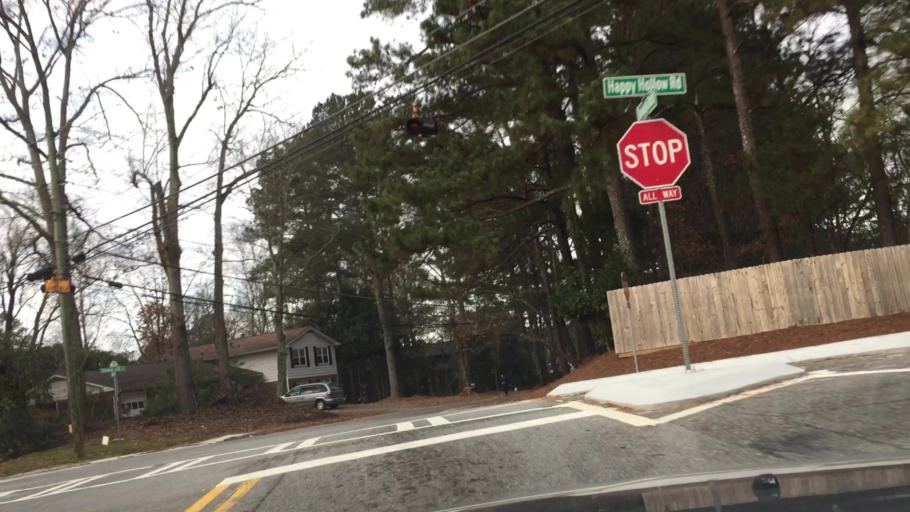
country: US
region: Georgia
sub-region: DeKalb County
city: Dunwoody
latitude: 33.9561
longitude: -84.2804
